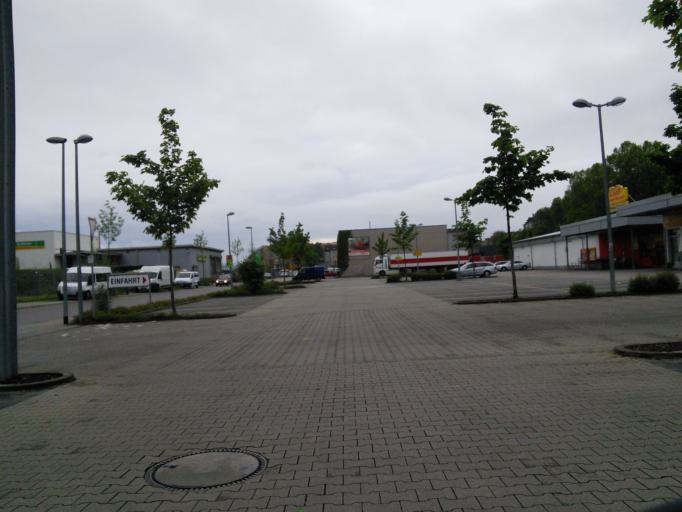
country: DE
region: Baden-Wuerttemberg
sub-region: Karlsruhe Region
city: Pforzheim
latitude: 48.8974
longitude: 8.7143
